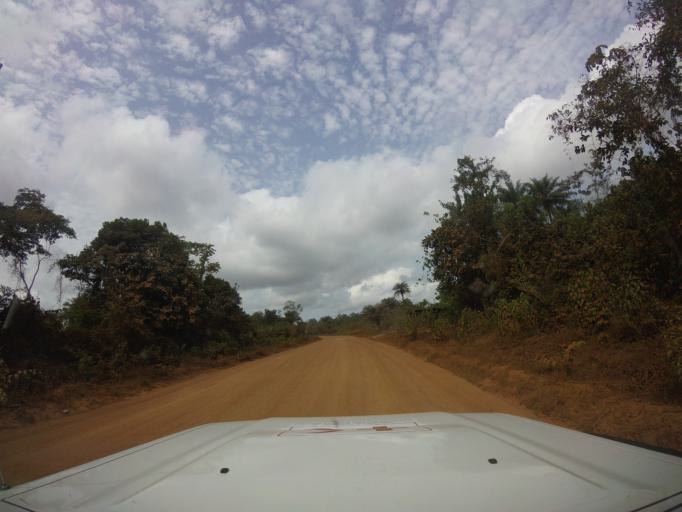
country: LR
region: Grand Cape Mount
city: Robertsport
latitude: 6.6805
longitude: -11.1347
